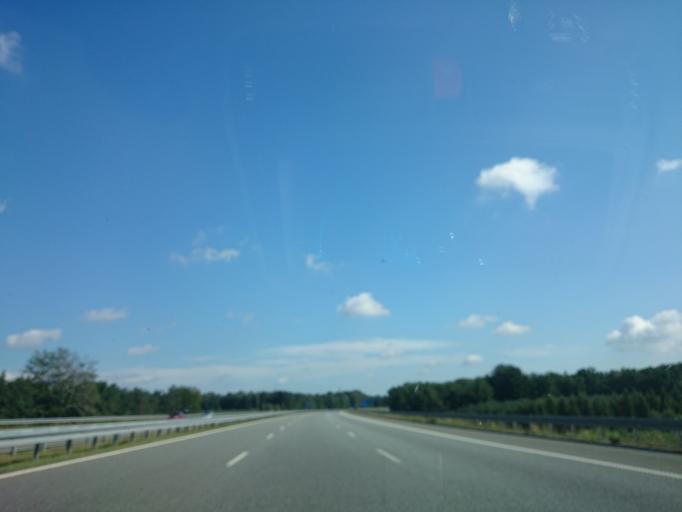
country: PL
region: Silesian Voivodeship
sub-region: Powiat rybnicki
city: Czerwionka-Leszczyny
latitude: 50.1460
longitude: 18.6962
